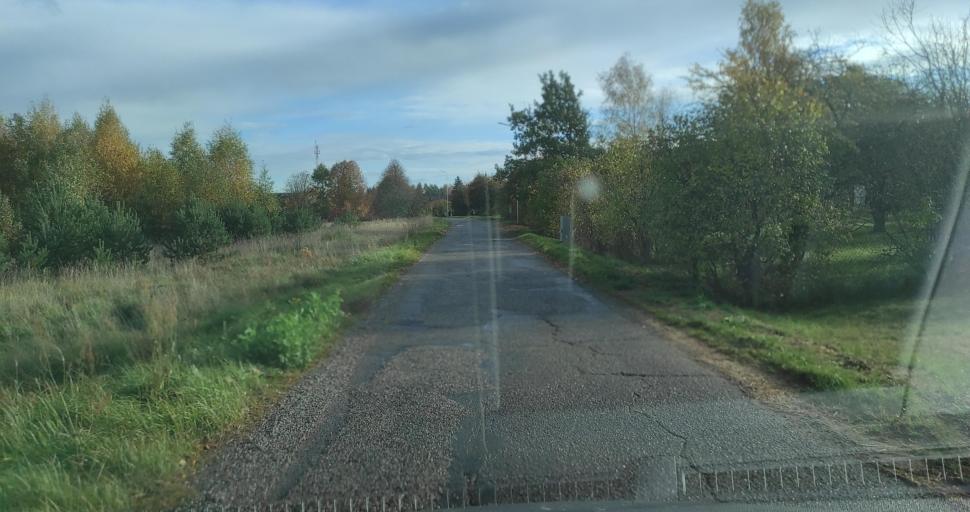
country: LV
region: Skrunda
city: Skrunda
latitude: 56.6825
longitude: 22.0509
